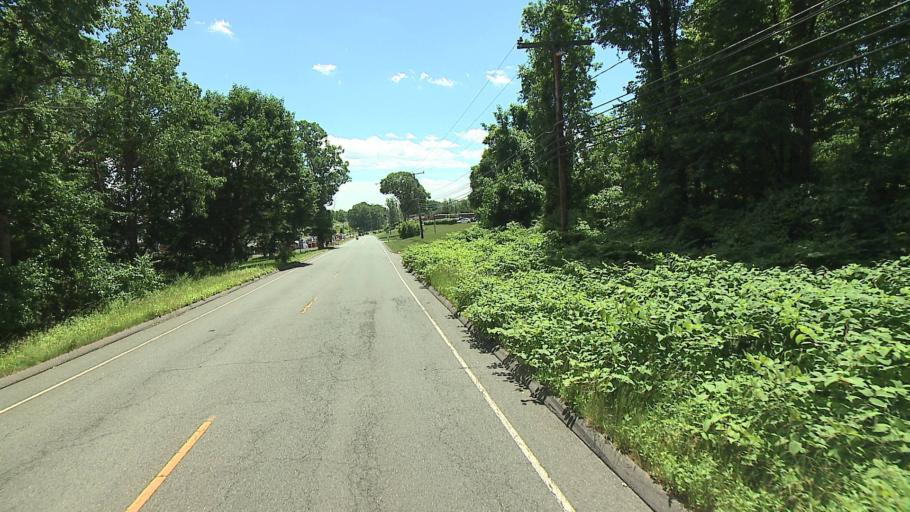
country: US
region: Connecticut
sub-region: Hartford County
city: Newington
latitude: 41.7016
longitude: -72.7061
